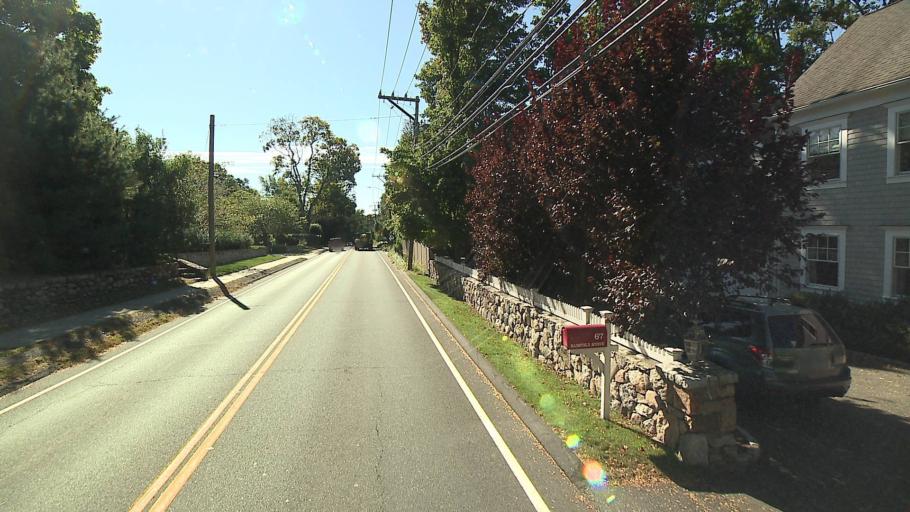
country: US
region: Connecticut
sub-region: Fairfield County
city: Darien
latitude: 41.0815
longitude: -73.4711
